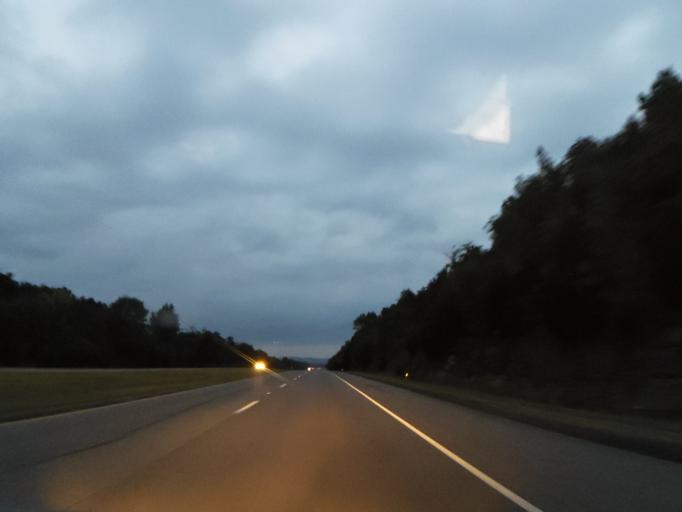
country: US
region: Alabama
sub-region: Madison County
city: New Hope
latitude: 34.6445
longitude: -86.3220
